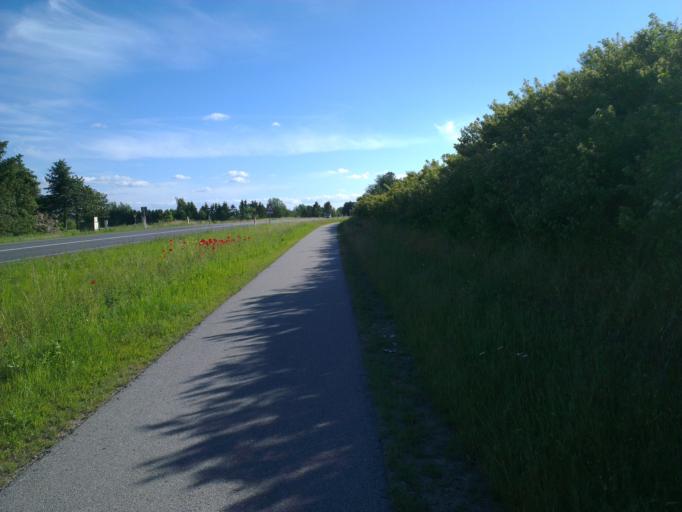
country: DK
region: Capital Region
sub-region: Frederikssund Kommune
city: Skibby
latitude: 55.7783
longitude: 11.9647
